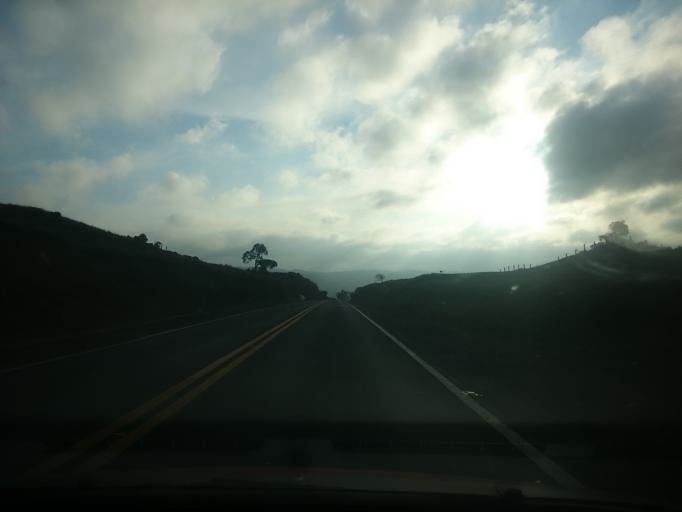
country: BR
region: Rio Grande do Sul
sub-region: Vacaria
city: Estrela
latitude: -28.1072
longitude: -50.6176
